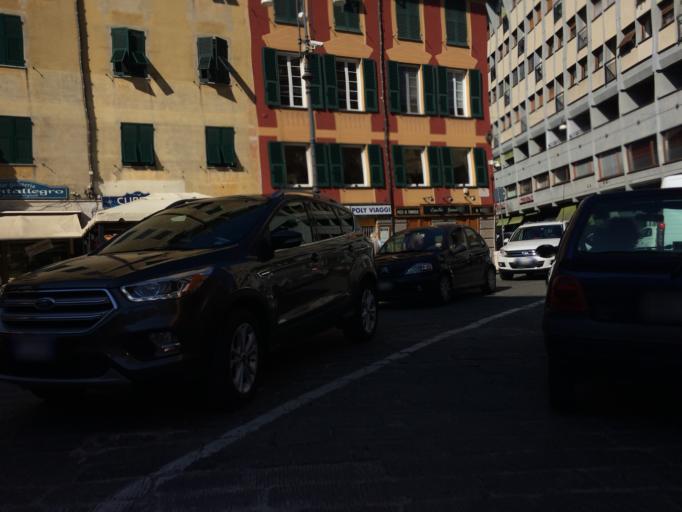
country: IT
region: Liguria
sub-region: Provincia di Genova
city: Rapallo
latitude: 44.3493
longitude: 9.2298
